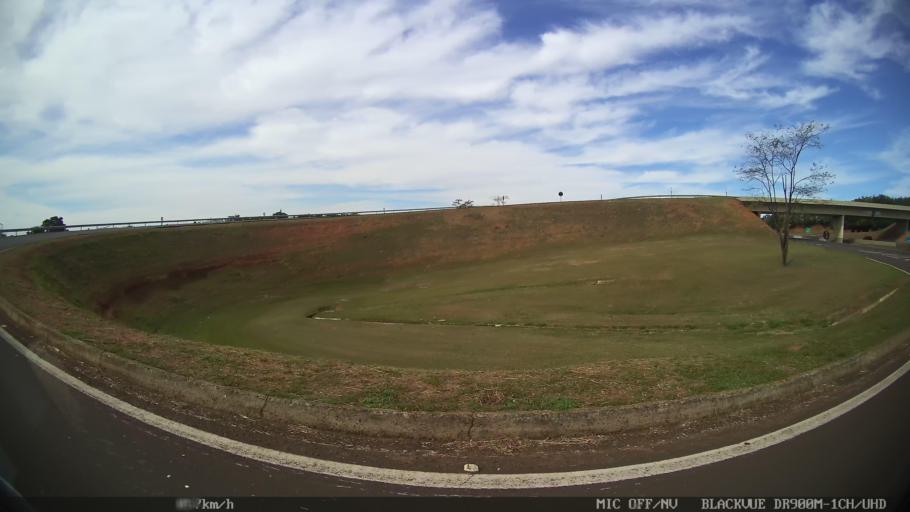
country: BR
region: Sao Paulo
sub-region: Matao
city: Matao
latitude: -21.6395
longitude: -48.3941
